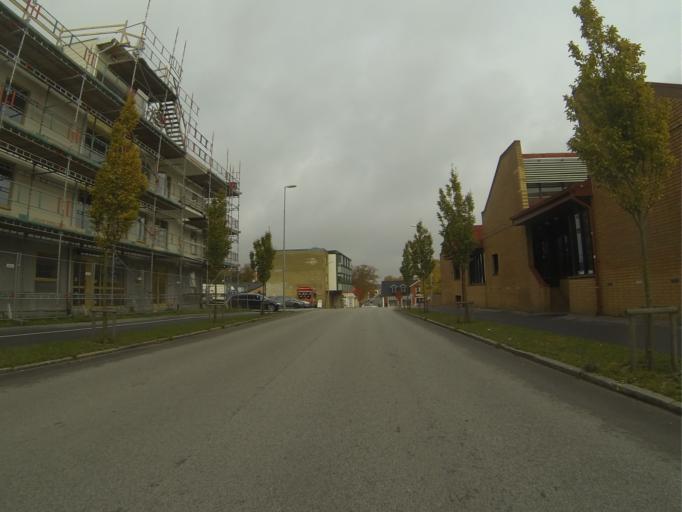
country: SE
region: Skane
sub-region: Sjobo Kommun
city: Sjoebo
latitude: 55.6308
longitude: 13.7050
